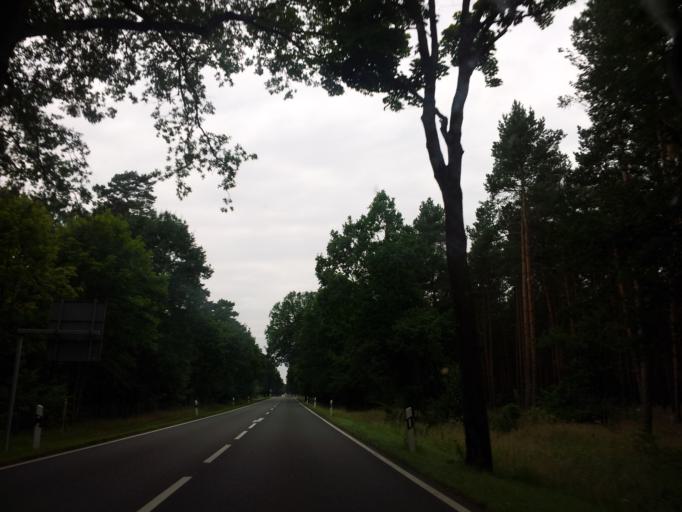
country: DE
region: Brandenburg
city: Niedergorsdorf
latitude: 52.0371
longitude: 12.9379
